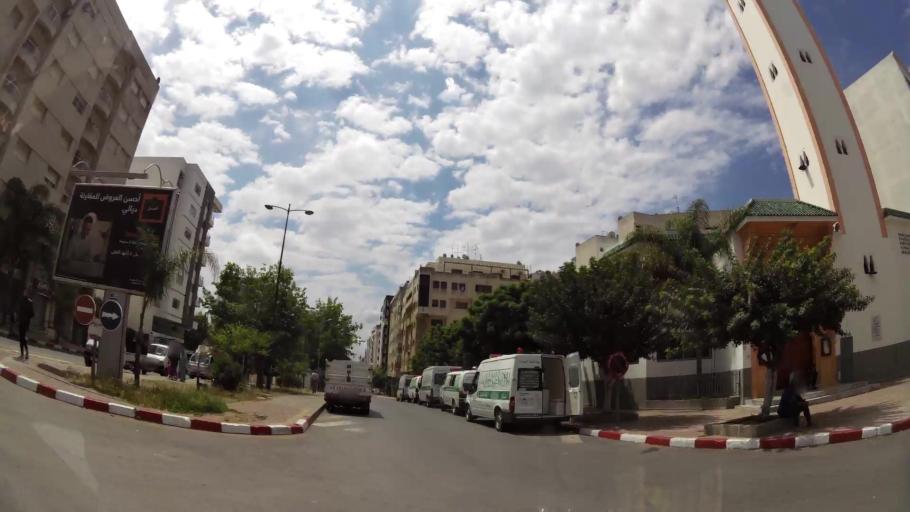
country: MA
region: Gharb-Chrarda-Beni Hssen
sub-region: Kenitra Province
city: Kenitra
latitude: 34.2602
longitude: -6.5898
